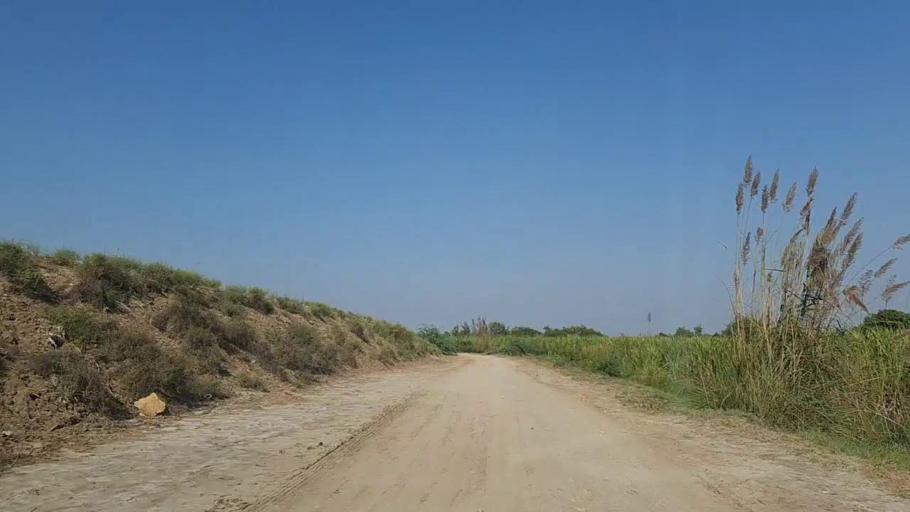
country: PK
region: Sindh
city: Chuhar Jamali
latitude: 24.5810
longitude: 68.0308
